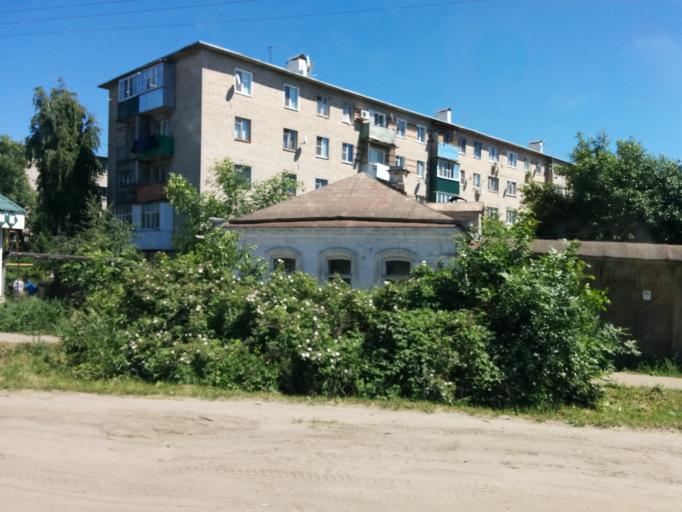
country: RU
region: Tambov
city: Morshansk
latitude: 53.4379
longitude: 41.8018
